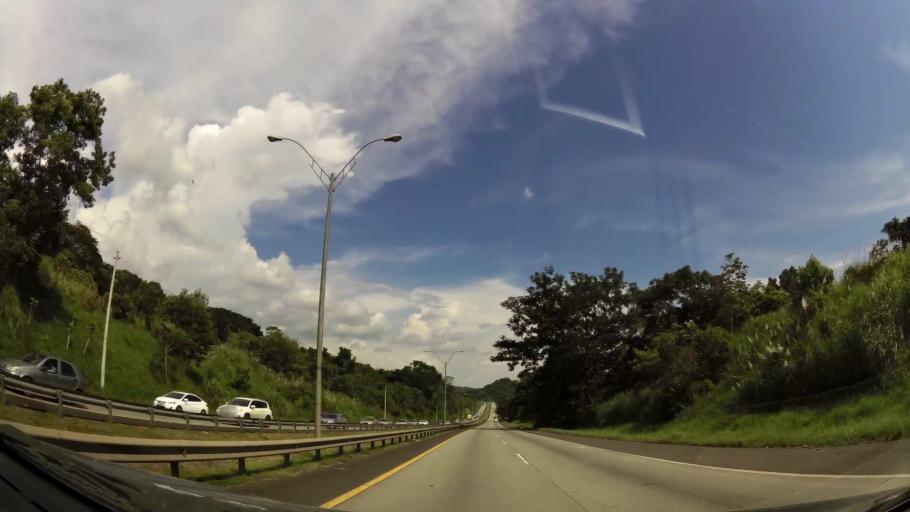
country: PA
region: Panama
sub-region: Distrito de Panama
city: Paraiso
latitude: 9.0274
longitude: -79.6018
